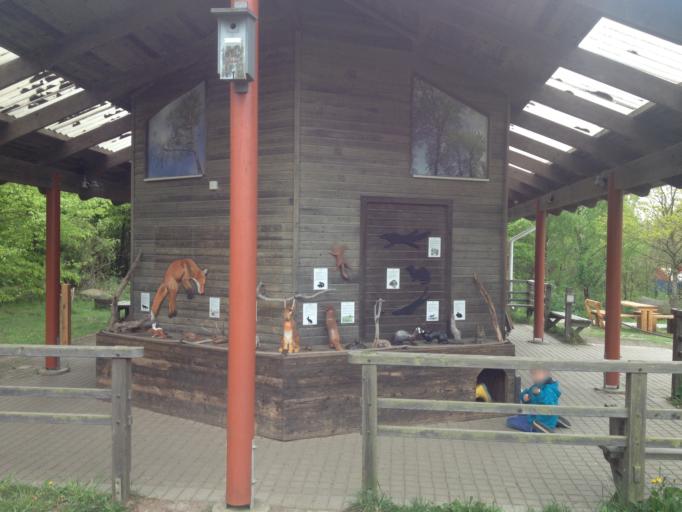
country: SE
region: Skane
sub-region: Lunds Kommun
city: Genarp
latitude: 55.6922
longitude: 13.3608
